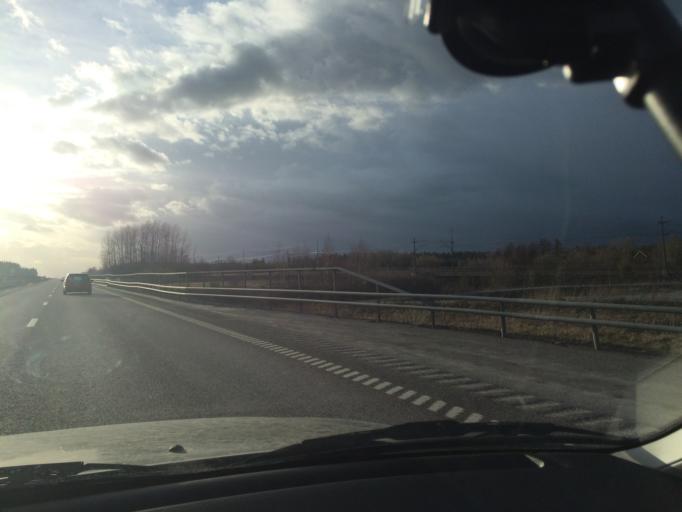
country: SE
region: Uppsala
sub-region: Enkopings Kommun
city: Enkoping
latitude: 59.6467
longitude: 17.0177
